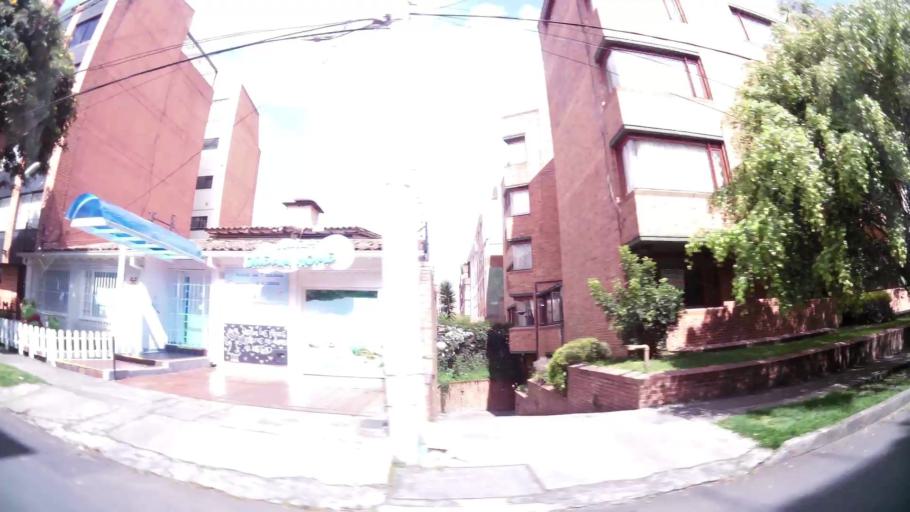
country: CO
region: Bogota D.C.
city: Barrio San Luis
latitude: 4.6951
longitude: -74.0393
